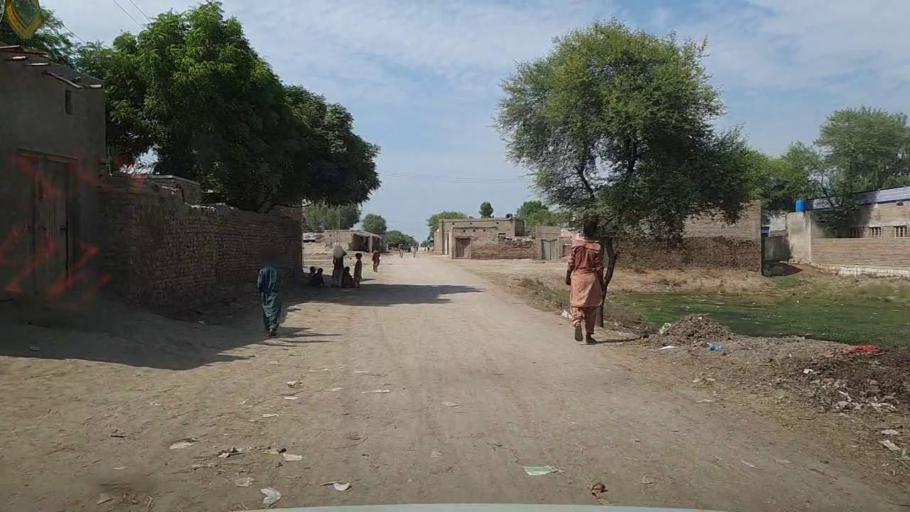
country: PK
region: Sindh
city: Thul
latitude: 28.2464
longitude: 68.8094
